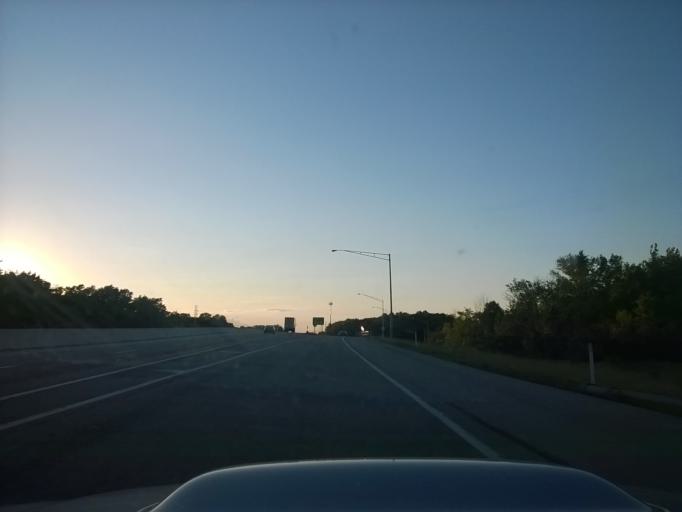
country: US
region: Indiana
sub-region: Marion County
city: Speedway
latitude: 39.8613
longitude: -86.2719
